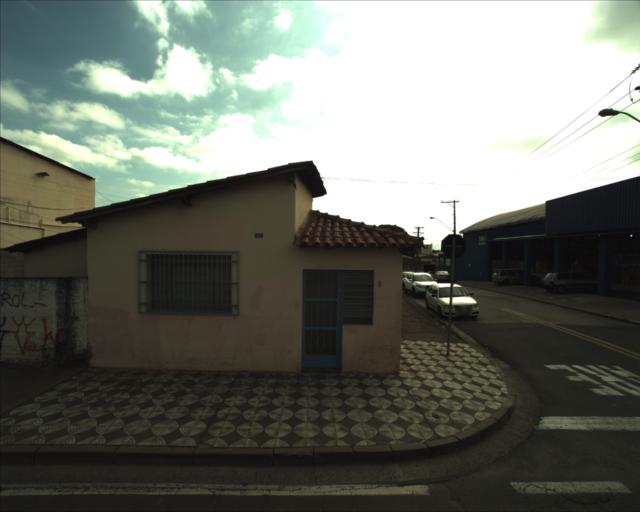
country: BR
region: Sao Paulo
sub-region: Sorocaba
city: Sorocaba
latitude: -23.5143
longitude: -47.4892
